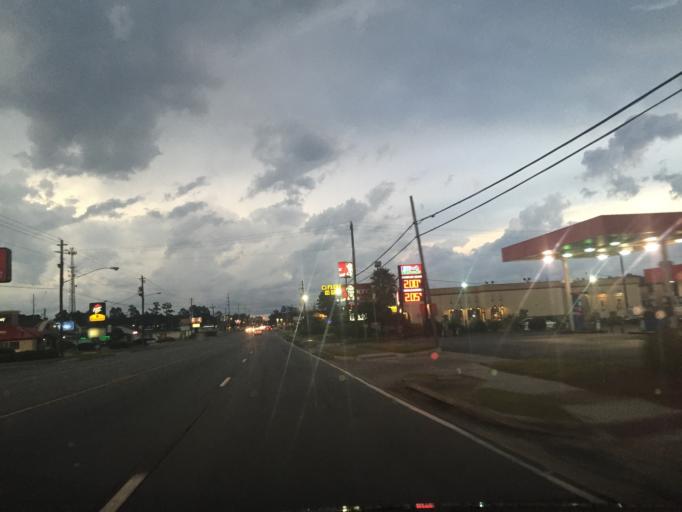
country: US
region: Georgia
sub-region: Liberty County
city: Hinesville
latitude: 31.8514
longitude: -81.5828
